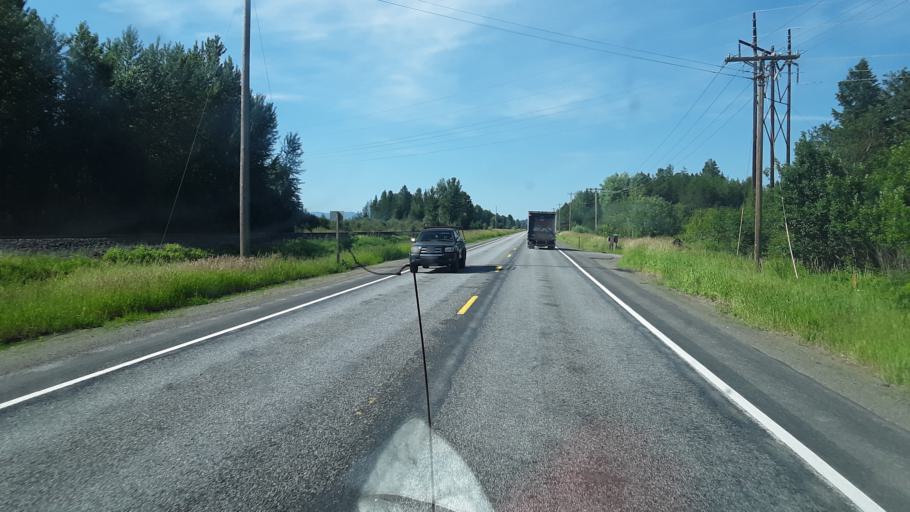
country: US
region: Idaho
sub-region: Bonner County
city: Ponderay
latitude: 48.4745
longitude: -116.4659
